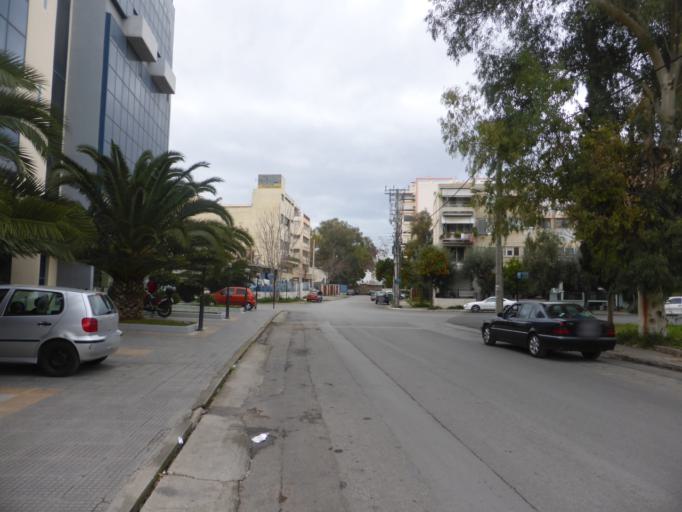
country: GR
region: Attica
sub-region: Nomarchia Athinas
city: Tavros
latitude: 37.9641
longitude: 23.6968
